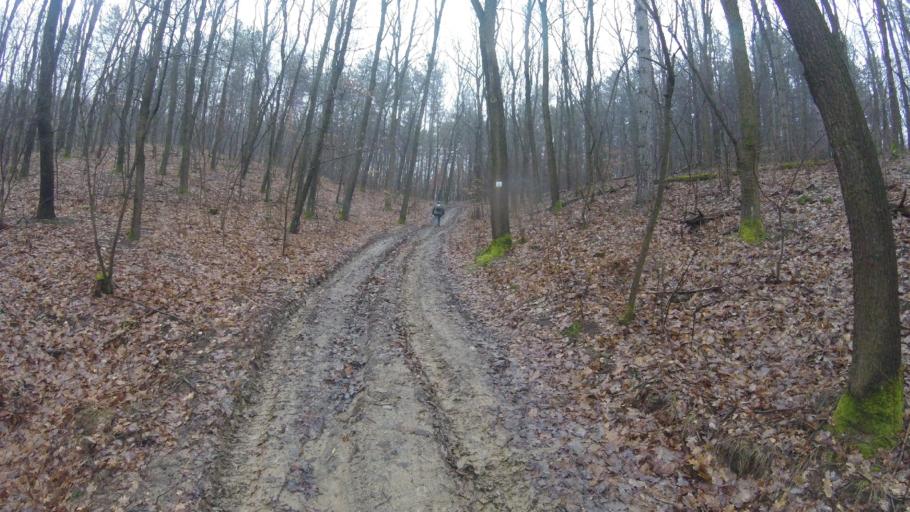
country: HU
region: Borsod-Abauj-Zemplen
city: Saly
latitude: 47.9674
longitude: 20.6169
